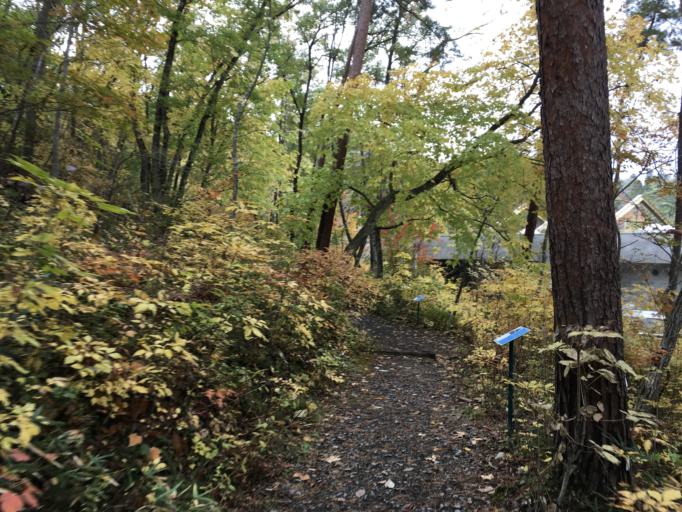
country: JP
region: Iwate
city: Hanamaki
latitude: 39.3974
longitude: 141.1693
